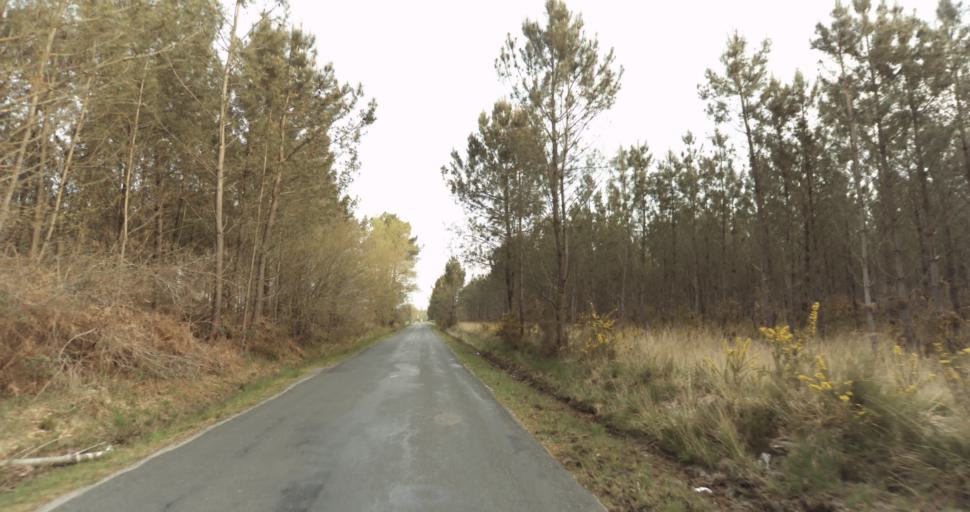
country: FR
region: Aquitaine
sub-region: Departement de la Gironde
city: Martignas-sur-Jalle
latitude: 44.8036
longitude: -0.7696
